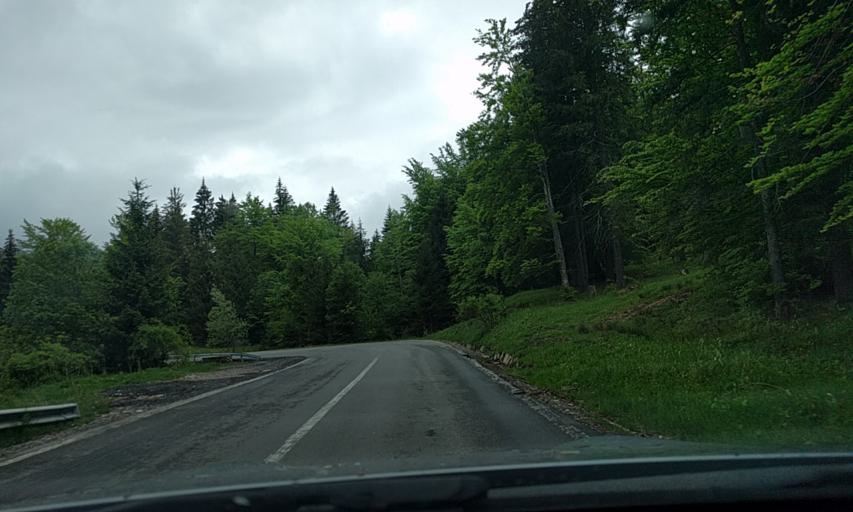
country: RO
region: Prahova
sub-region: Oras Sinaia
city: Sinaia
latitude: 45.3041
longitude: 25.5198
